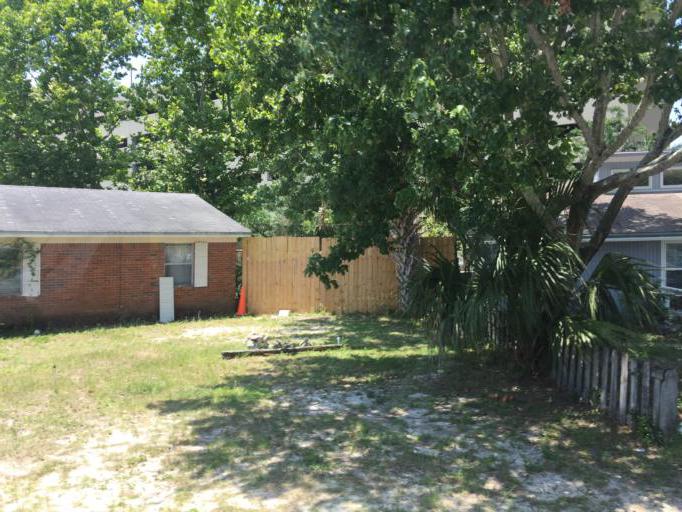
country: US
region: Florida
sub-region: Bay County
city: Panama City Beach
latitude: 30.2093
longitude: -85.8579
